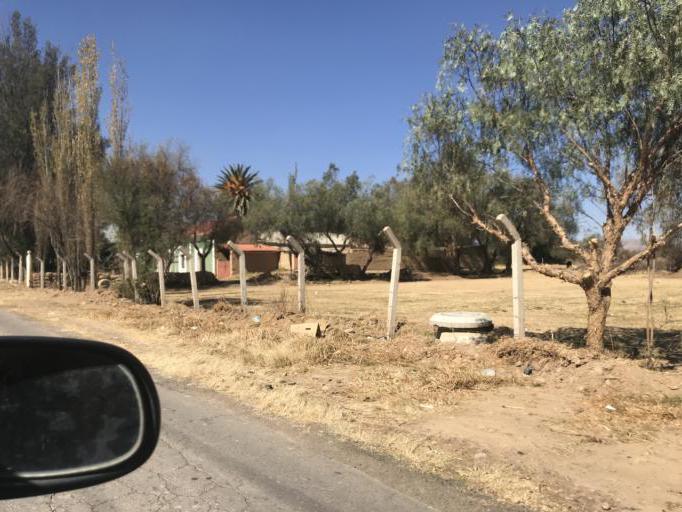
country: BO
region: Cochabamba
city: Cliza
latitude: -17.5970
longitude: -65.9539
